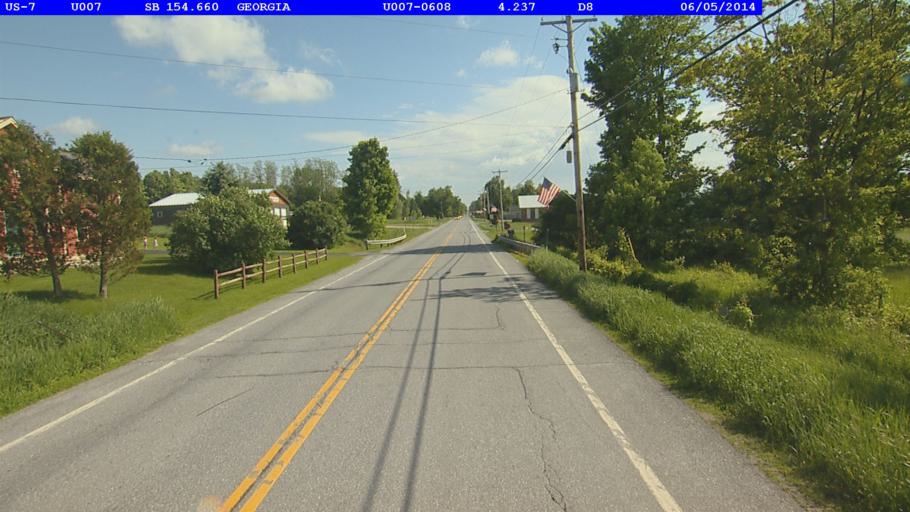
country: US
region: Vermont
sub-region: Franklin County
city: Saint Albans
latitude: 44.7324
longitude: -73.1168
